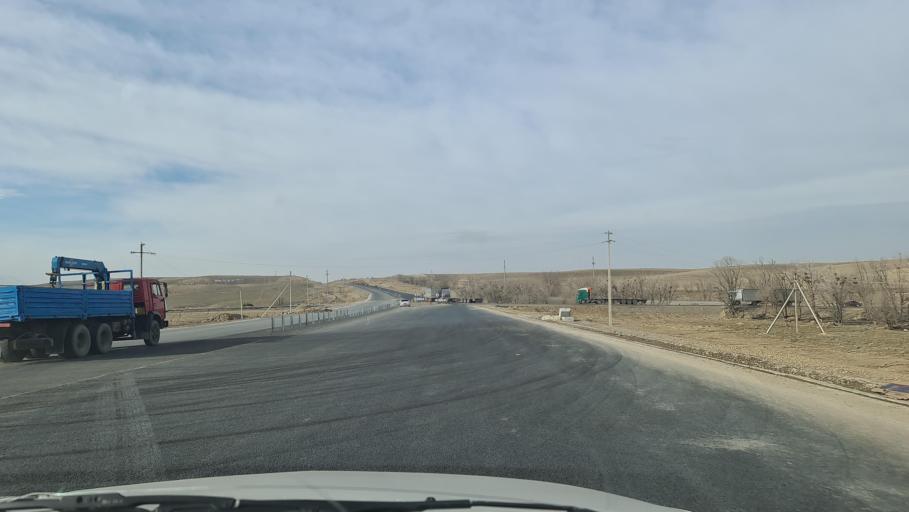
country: KG
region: Chuy
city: Bystrovka
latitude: 43.3208
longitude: 76.0640
